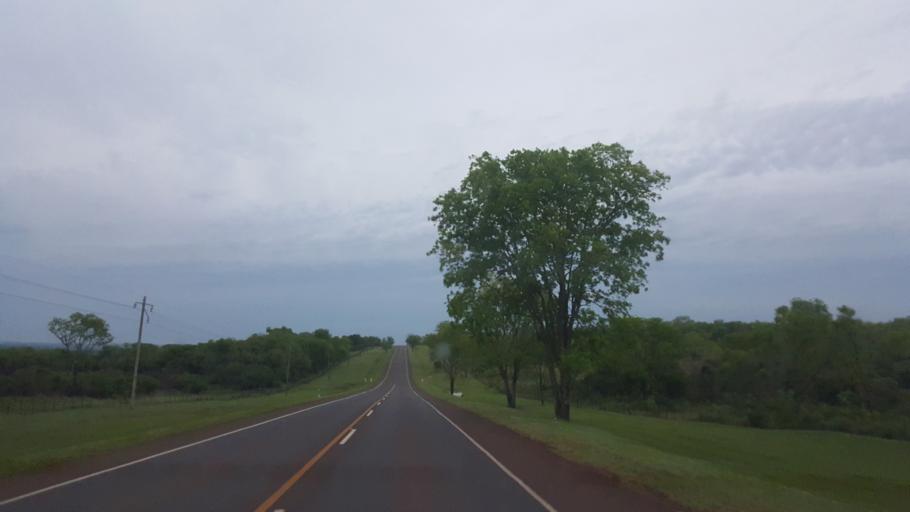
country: AR
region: Misiones
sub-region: Departamento de Apostoles
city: San Jose
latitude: -27.7219
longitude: -55.7917
